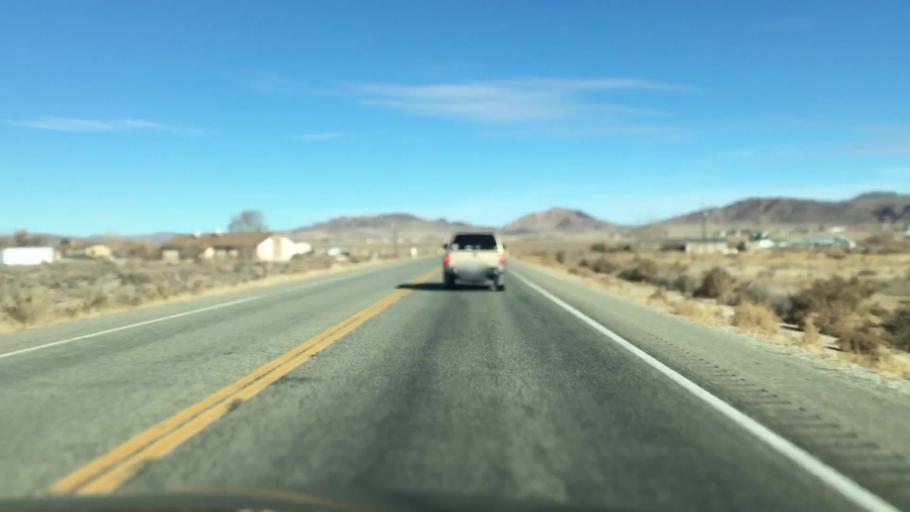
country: US
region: Nevada
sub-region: Lyon County
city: Yerington
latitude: 39.0115
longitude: -119.0759
